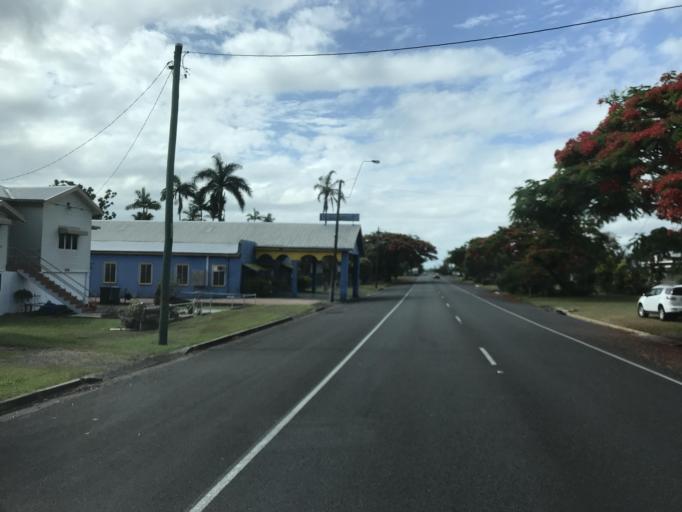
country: AU
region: Queensland
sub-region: Cassowary Coast
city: Innisfail
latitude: -17.5395
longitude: 146.0327
